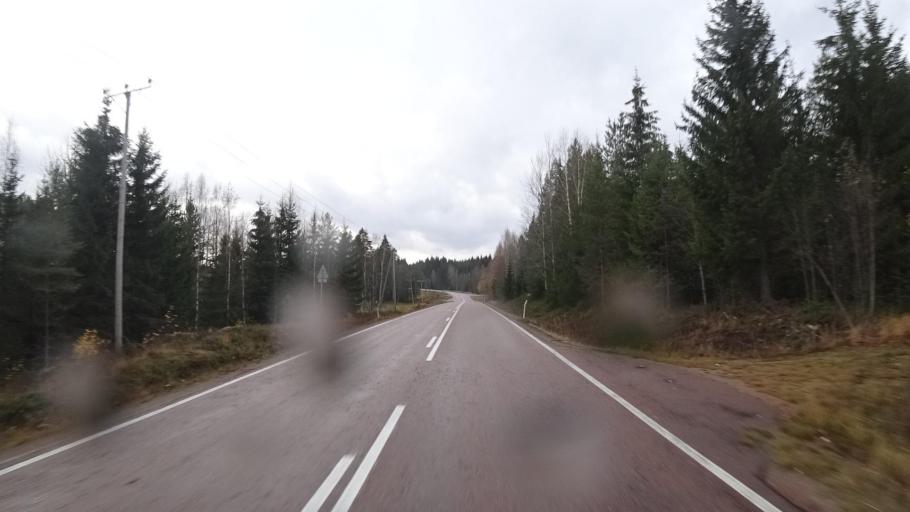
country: FI
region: Southern Savonia
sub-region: Mikkeli
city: Kangasniemi
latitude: 62.0665
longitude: 26.6584
